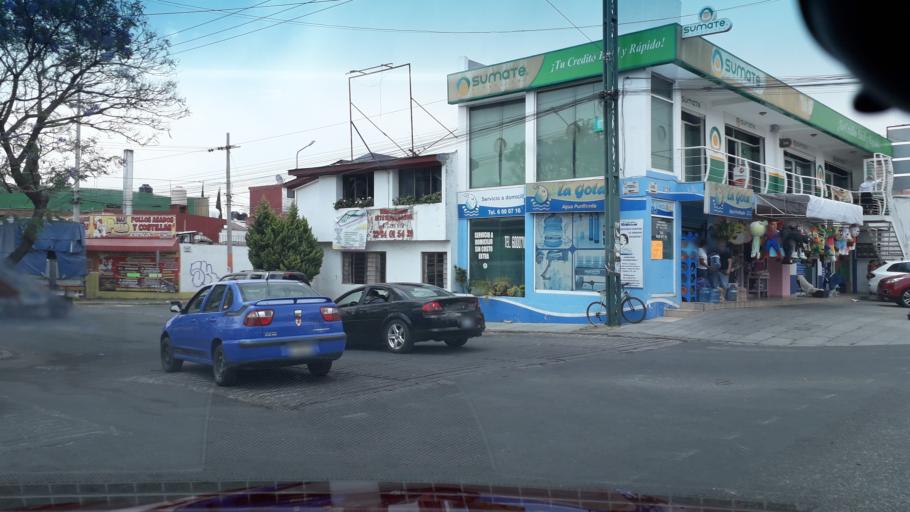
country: MX
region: Puebla
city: Puebla
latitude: 19.0051
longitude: -98.2339
